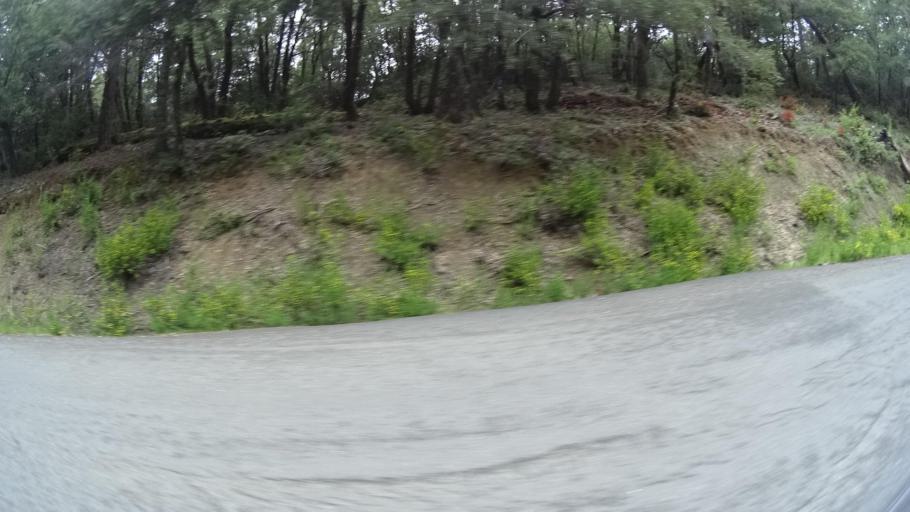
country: US
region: California
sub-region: Humboldt County
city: Redway
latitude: 40.2791
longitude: -123.7964
